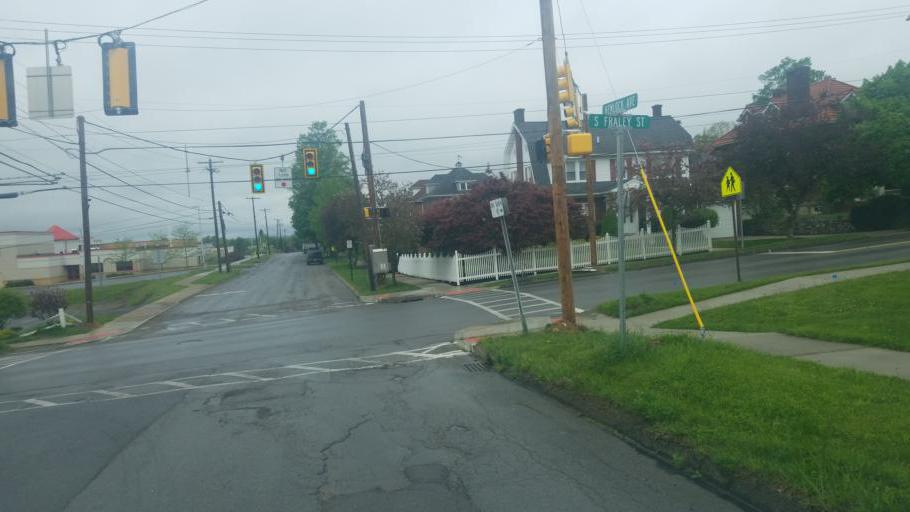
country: US
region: Pennsylvania
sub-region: McKean County
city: Kane
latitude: 41.6558
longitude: -78.8107
